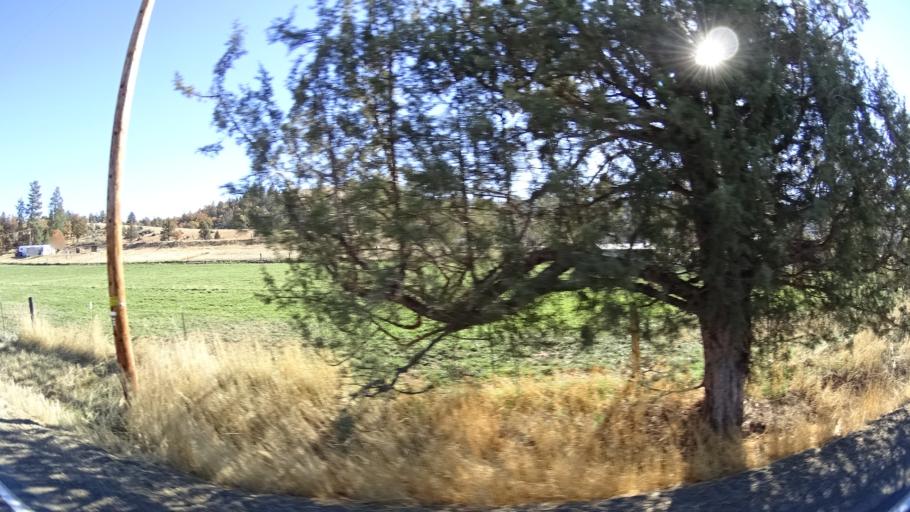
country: US
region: California
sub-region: Siskiyou County
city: Yreka
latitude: 41.5544
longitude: -122.8281
